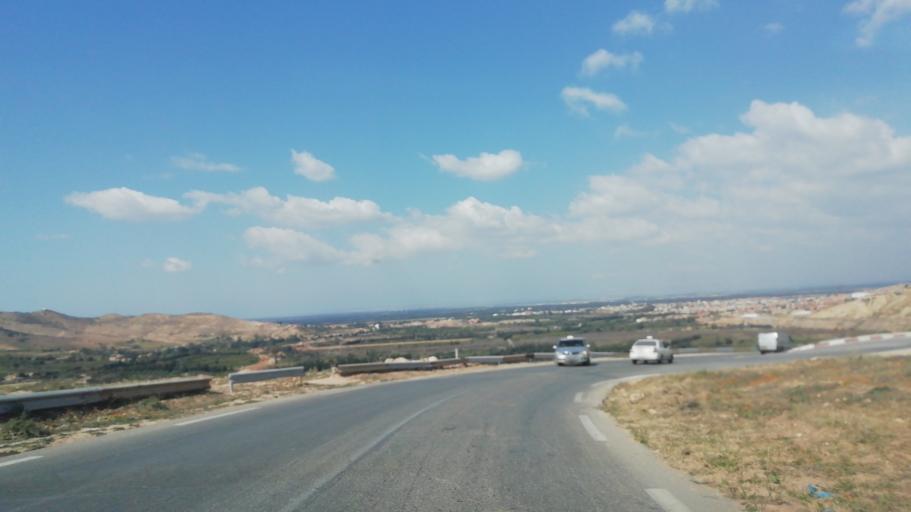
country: DZ
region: Mascara
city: Mascara
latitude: 35.5559
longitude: 0.0667
